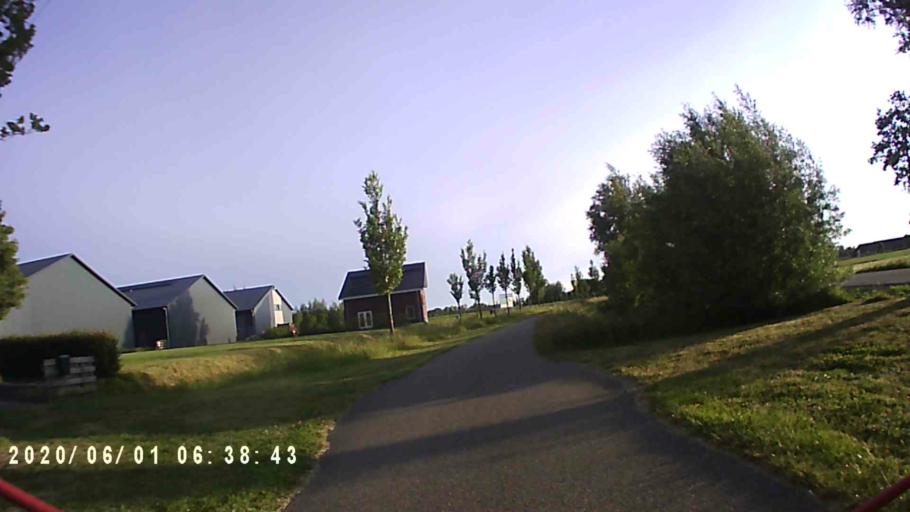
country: NL
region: Friesland
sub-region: Gemeente Kollumerland en Nieuwkruisland
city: Kollum
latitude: 53.2875
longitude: 6.1581
